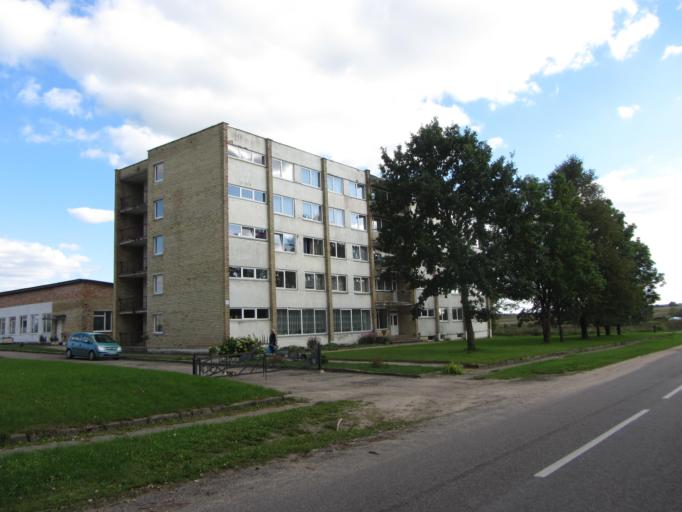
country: LT
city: Salcininkai
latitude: 54.1875
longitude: 25.6221
